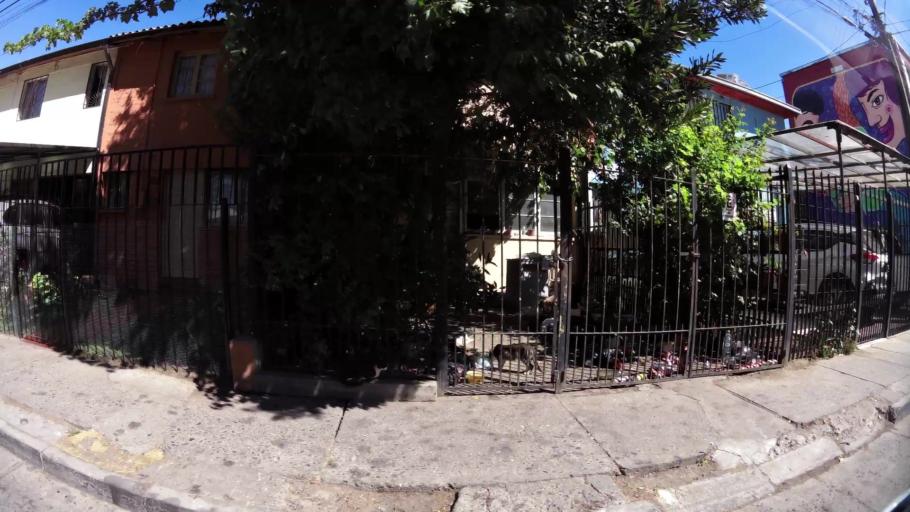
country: CL
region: O'Higgins
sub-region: Provincia de Cachapoal
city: Rancagua
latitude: -34.1815
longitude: -70.7401
